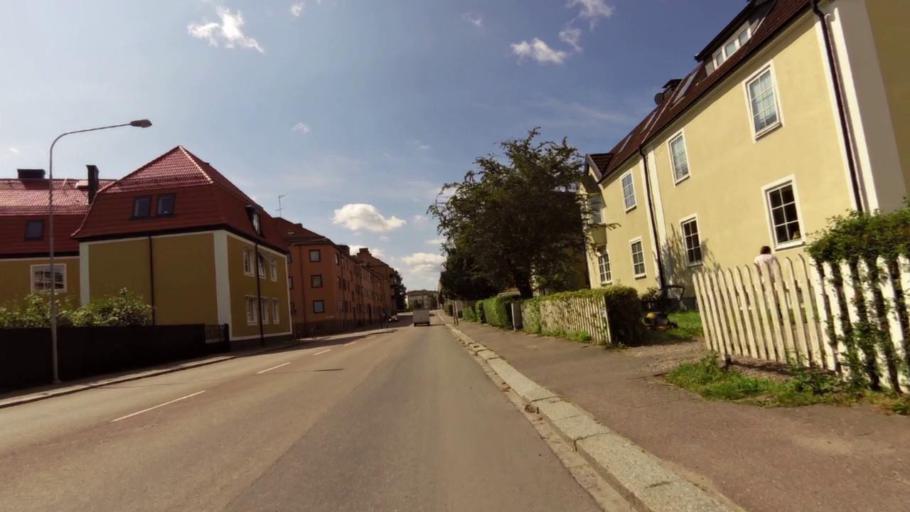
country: SE
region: OEstergoetland
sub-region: Linkopings Kommun
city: Linkoping
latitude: 58.4179
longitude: 15.6149
